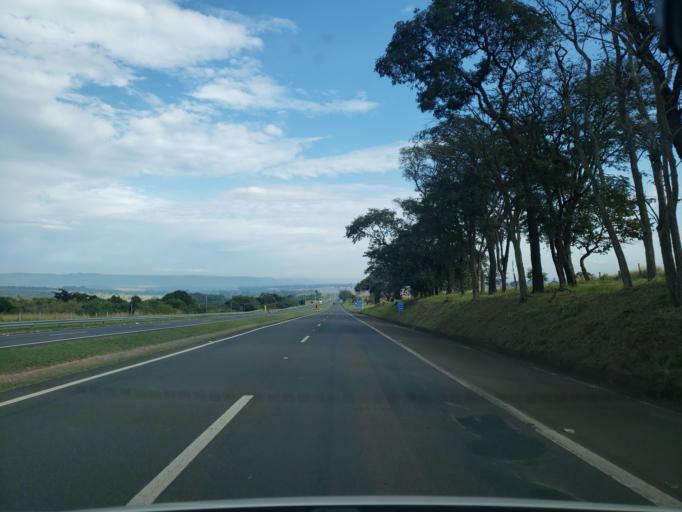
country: BR
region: Sao Paulo
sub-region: Brotas
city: Brotas
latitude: -22.2664
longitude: -48.1515
